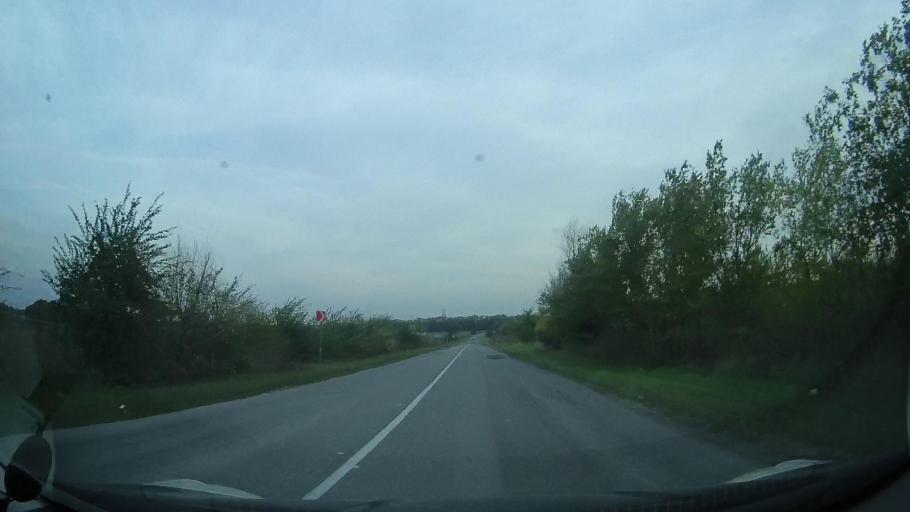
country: RU
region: Rostov
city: Ol'ginskaya
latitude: 47.1181
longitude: 39.9743
